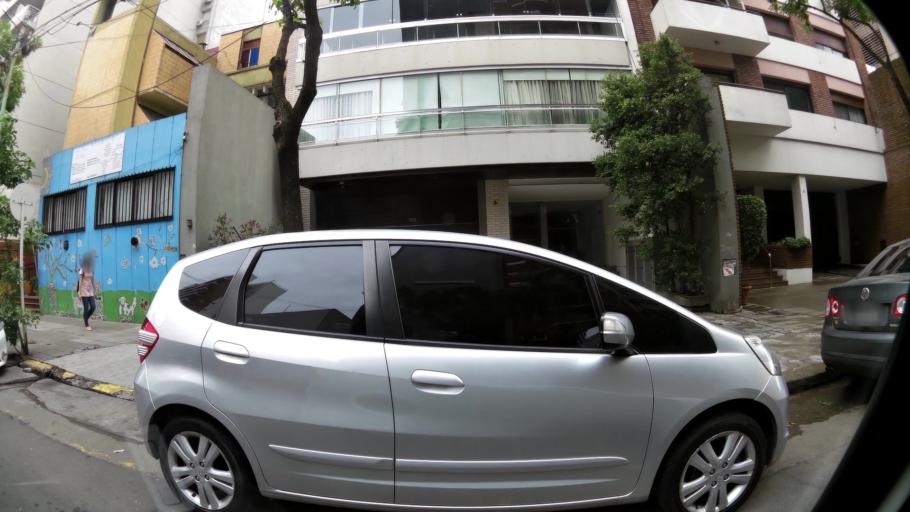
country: AR
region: Buenos Aires F.D.
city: Colegiales
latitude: -34.5509
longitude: -58.4537
